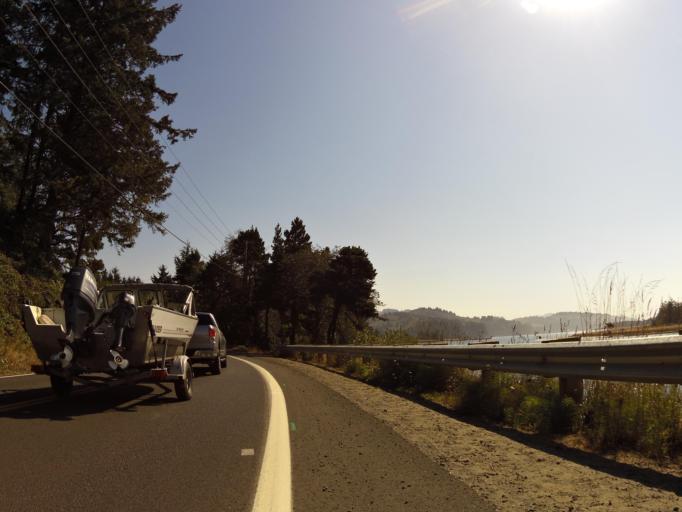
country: US
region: Oregon
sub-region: Tillamook County
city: Pacific City
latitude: 45.1921
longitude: -123.9551
